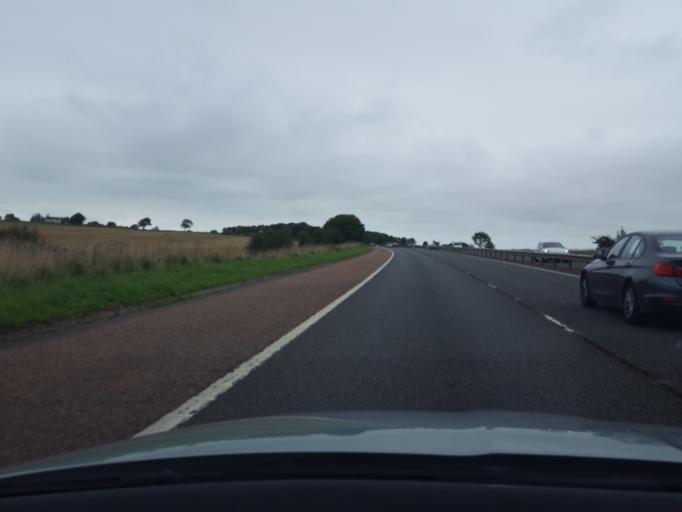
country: GB
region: Scotland
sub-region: Perth and Kinross
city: Milnathort
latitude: 56.2446
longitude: -3.3829
